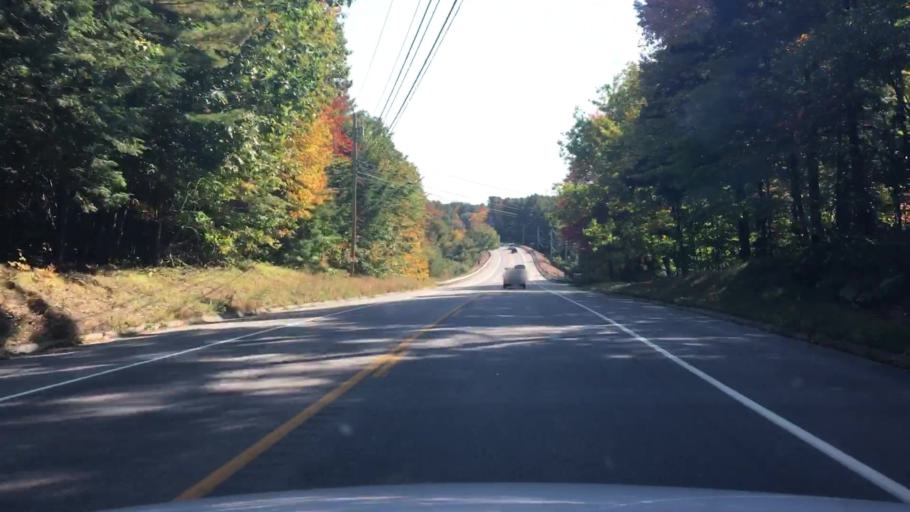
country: US
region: Maine
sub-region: Androscoggin County
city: Lisbon Falls
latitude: 43.9659
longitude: -70.0183
